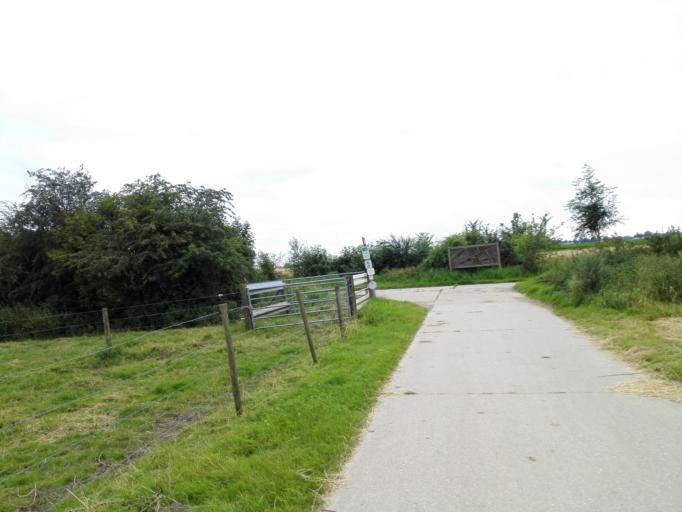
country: BE
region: Flanders
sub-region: Provincie Vlaams-Brabant
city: Tienen
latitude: 50.8068
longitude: 4.9881
